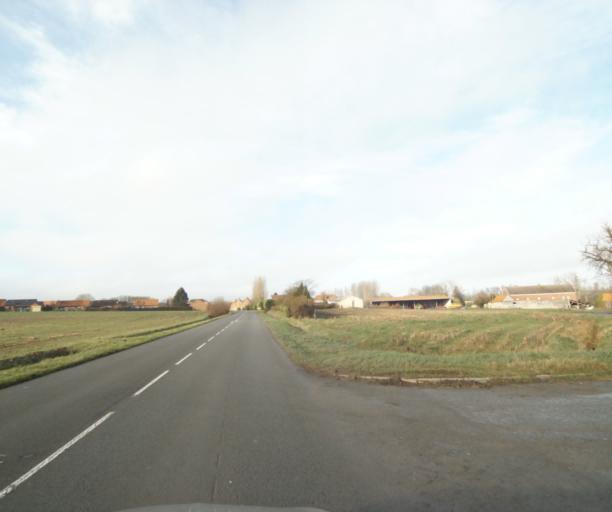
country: FR
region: Nord-Pas-de-Calais
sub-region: Departement du Nord
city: Vendegies-sur-Ecaillon
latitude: 50.2637
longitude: 3.4842
